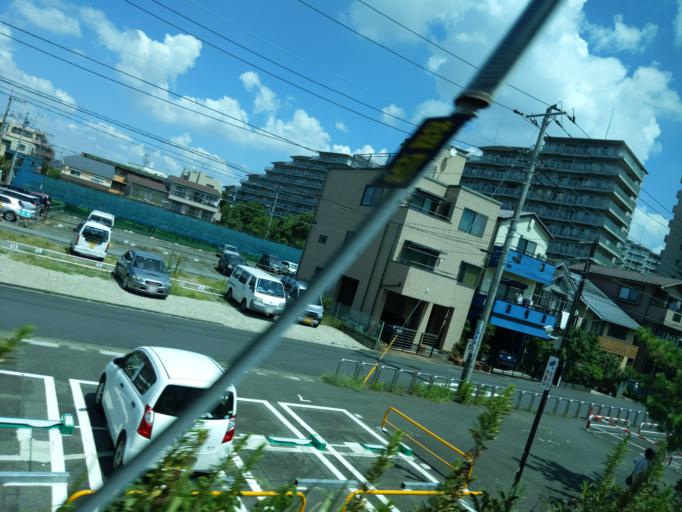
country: JP
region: Tokyo
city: Chofugaoka
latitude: 35.6309
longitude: 139.5474
